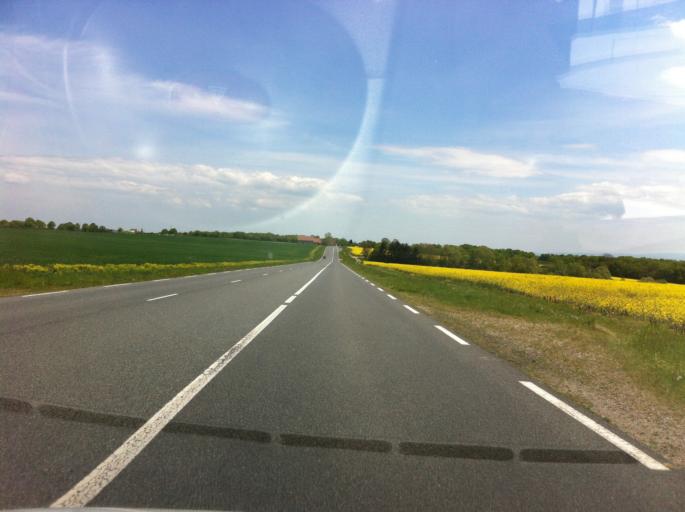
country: FR
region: Auvergne
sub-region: Departement de l'Allier
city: Chantelle
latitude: 46.3172
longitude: 3.1635
